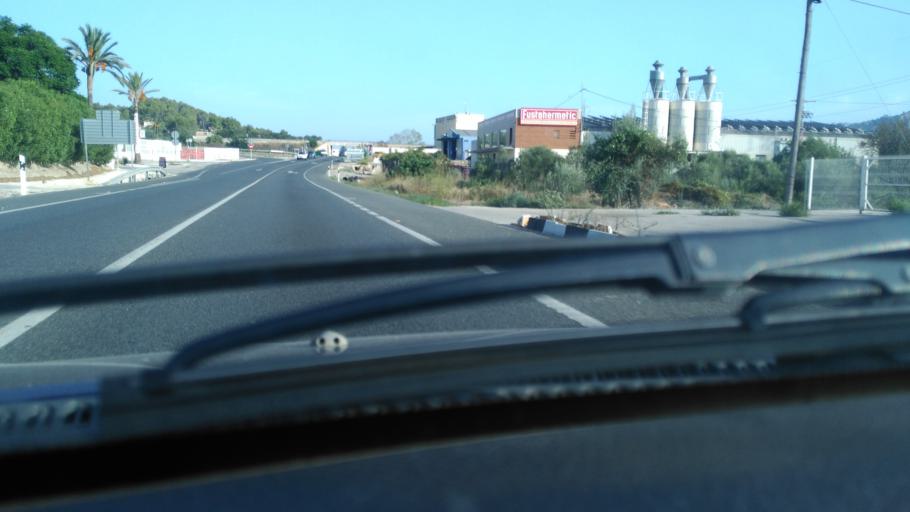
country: ES
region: Valencia
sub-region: Provincia de Alicante
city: Pedreguer
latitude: 38.8052
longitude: 0.0386
